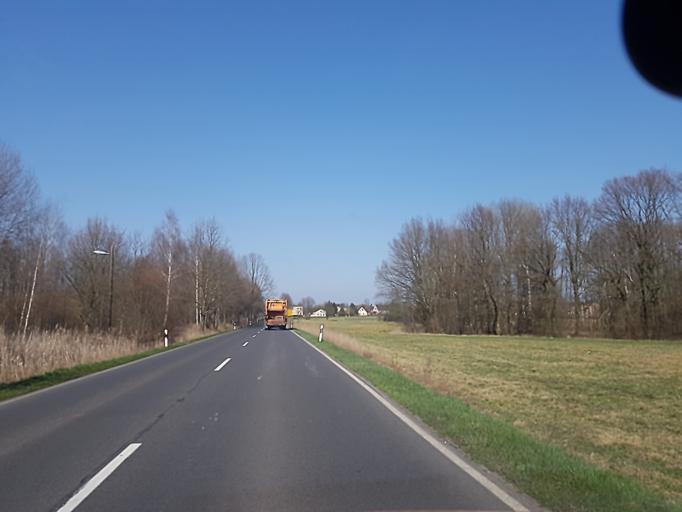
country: DE
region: Brandenburg
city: Forst
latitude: 51.6874
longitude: 14.6010
